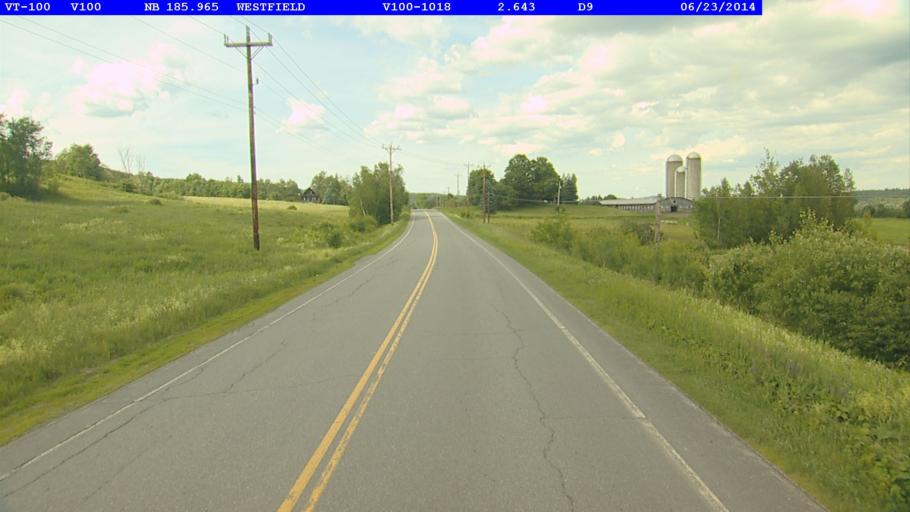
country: US
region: Vermont
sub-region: Orleans County
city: Newport
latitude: 44.8728
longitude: -72.4317
